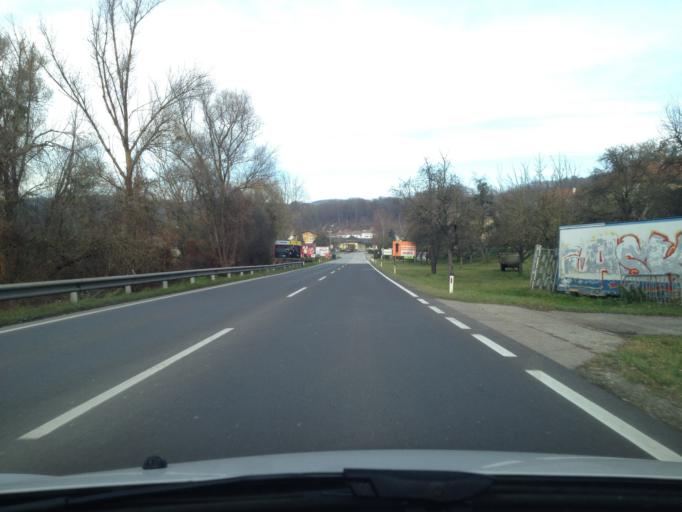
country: AT
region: Upper Austria
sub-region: Politischer Bezirk Urfahr-Umgebung
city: Steyregg
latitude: 48.3172
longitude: 14.3382
